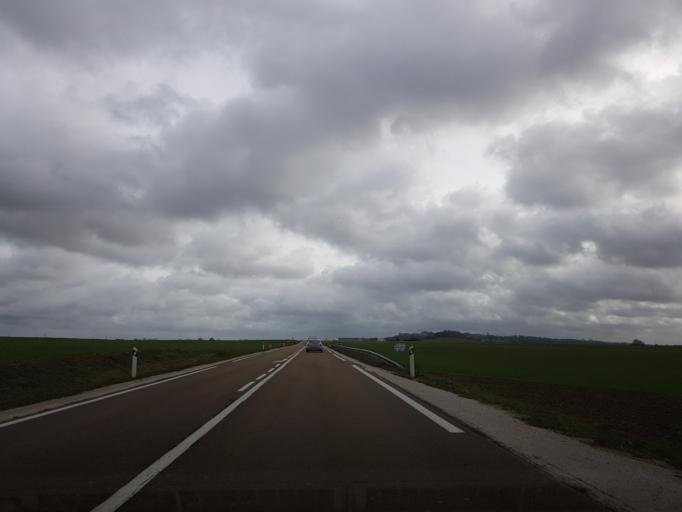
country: FR
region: Champagne-Ardenne
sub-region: Departement de la Haute-Marne
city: Langres
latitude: 47.8984
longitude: 5.3088
